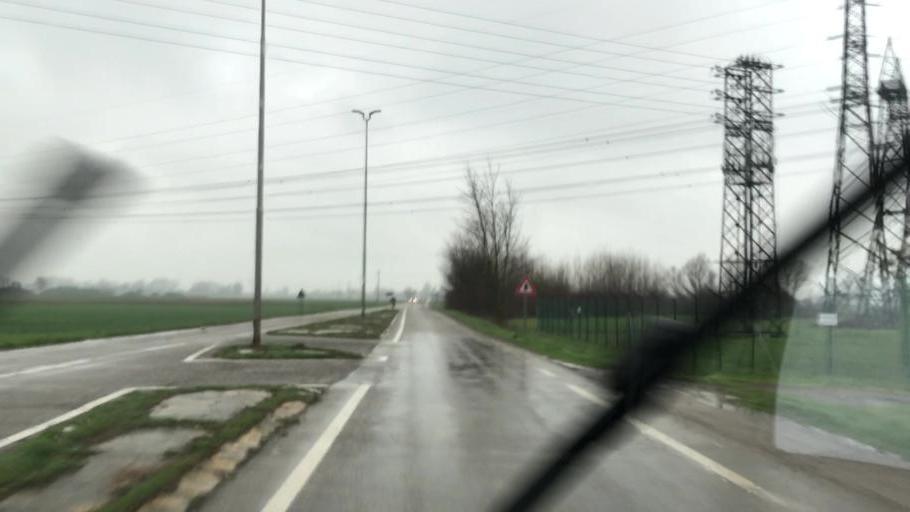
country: IT
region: Lombardy
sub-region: Provincia di Mantova
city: Carbonara di Po
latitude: 45.0214
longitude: 11.2505
